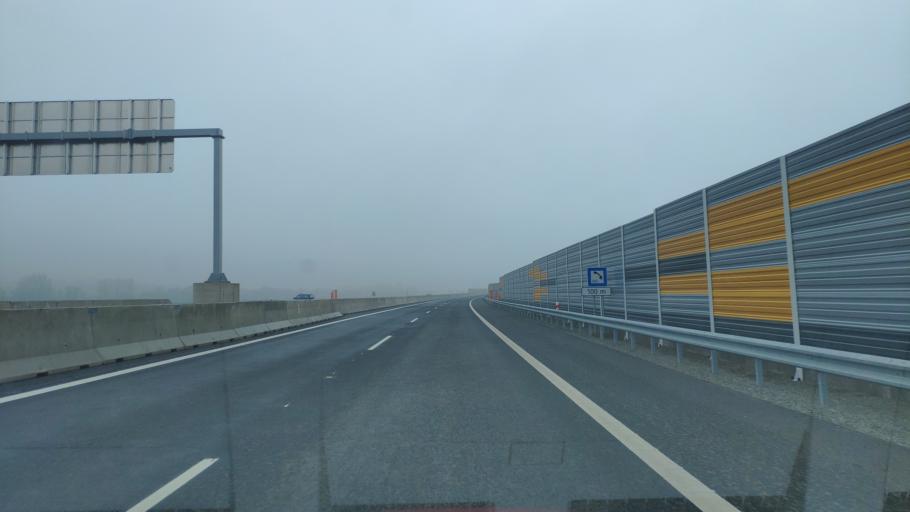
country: SK
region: Kosicky
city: Kosice
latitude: 48.7595
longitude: 21.3281
